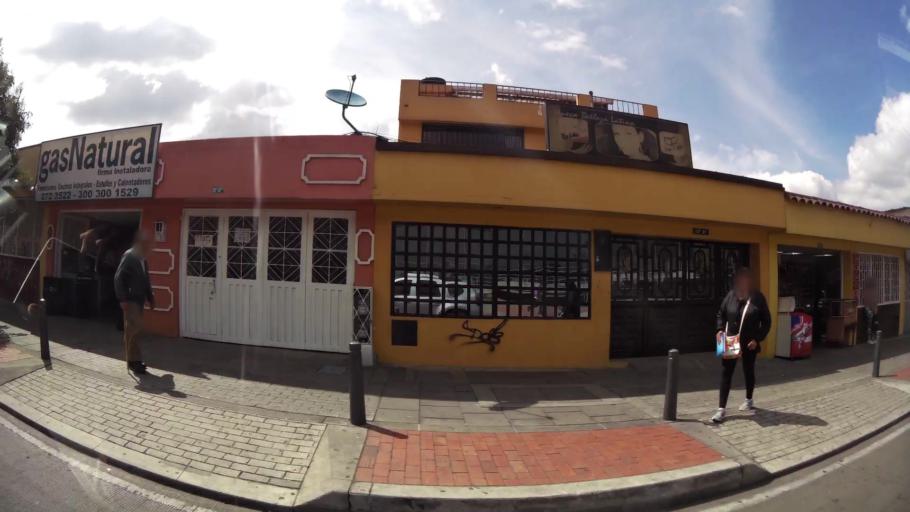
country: CO
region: Bogota D.C.
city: Bogota
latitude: 4.5661
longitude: -74.0975
